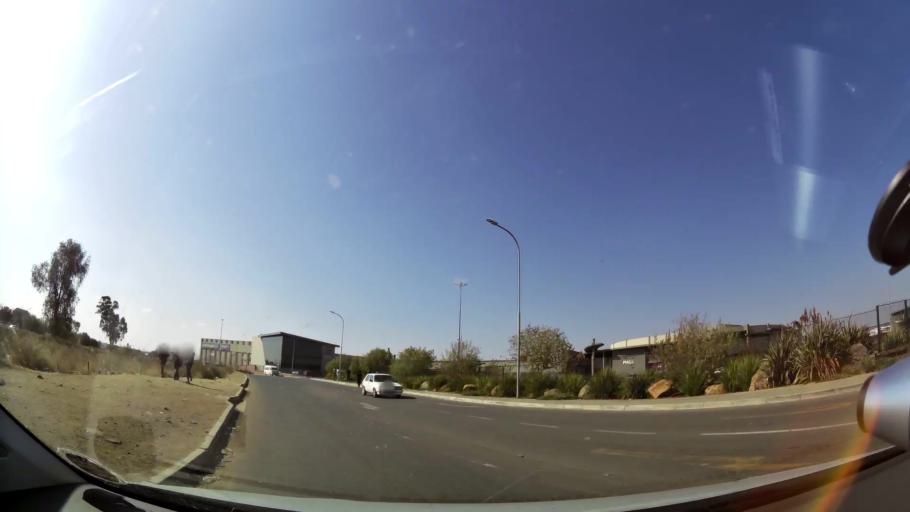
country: ZA
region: Orange Free State
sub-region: Mangaung Metropolitan Municipality
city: Bloemfontein
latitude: -29.1578
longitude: 26.2550
